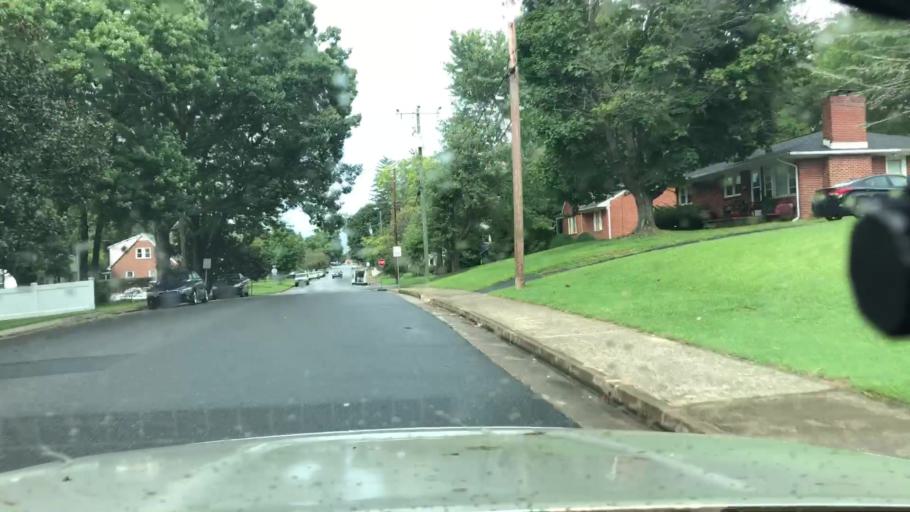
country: US
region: Virginia
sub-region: City of Waynesboro
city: Waynesboro
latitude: 38.0666
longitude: -78.9041
